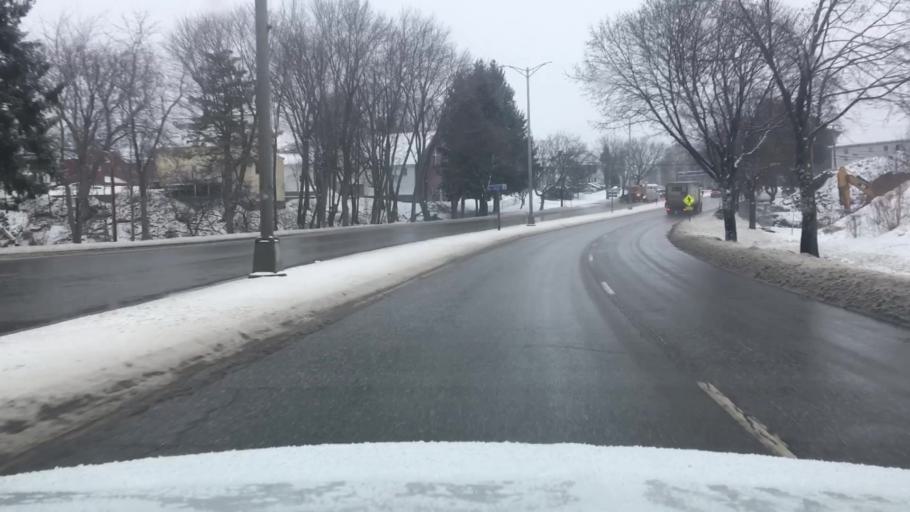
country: US
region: Maine
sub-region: Androscoggin County
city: Auburn
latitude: 44.1011
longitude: -70.2285
